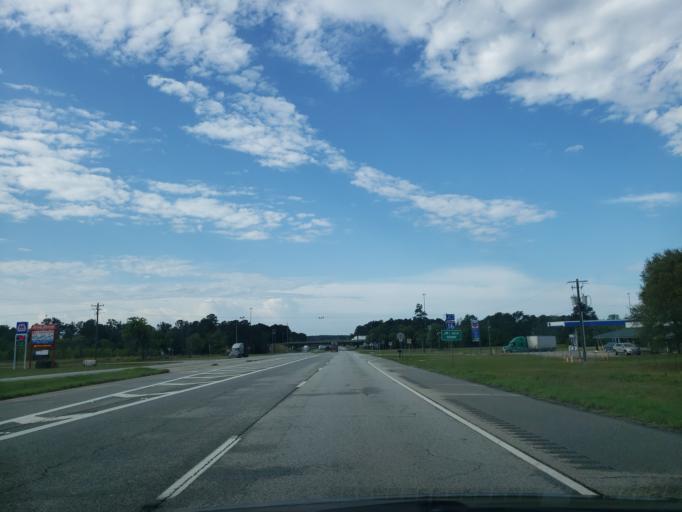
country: US
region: Georgia
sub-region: Emanuel County
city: Swainsboro
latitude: 32.4045
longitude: -82.3057
